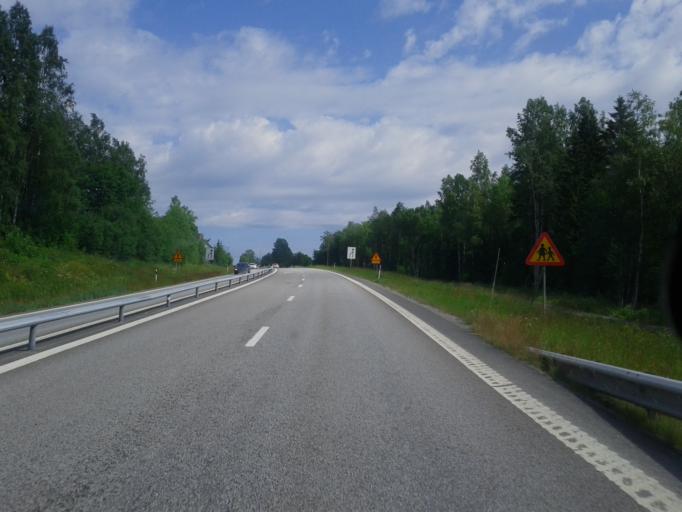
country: SE
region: Vaesternorrland
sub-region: OErnskoeldsviks Kommun
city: Ornskoldsvik
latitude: 63.2981
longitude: 18.8952
